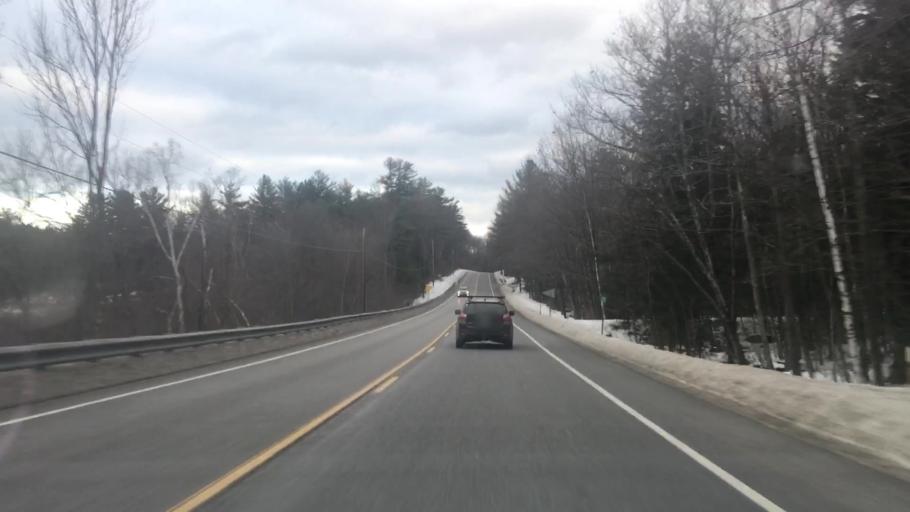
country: US
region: New Hampshire
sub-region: Hillsborough County
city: Antrim
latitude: 43.0769
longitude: -72.0030
